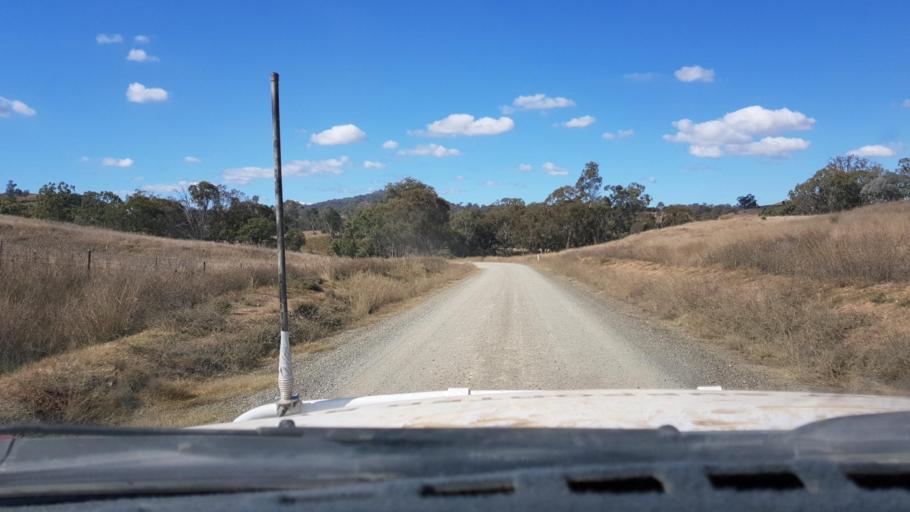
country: AU
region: New South Wales
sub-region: Tamworth Municipality
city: Manilla
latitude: -30.4521
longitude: 150.7348
